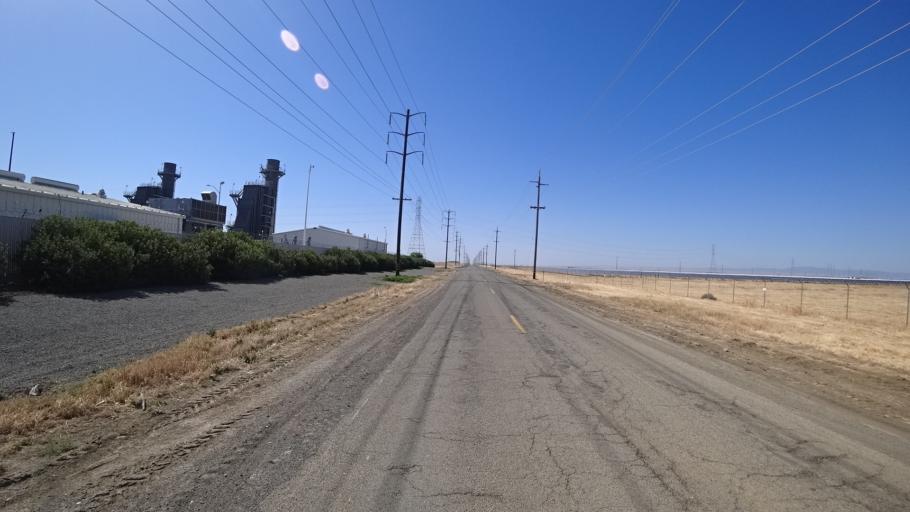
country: US
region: California
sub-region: Kings County
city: Lemoore Station
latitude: 36.2405
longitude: -119.9052
